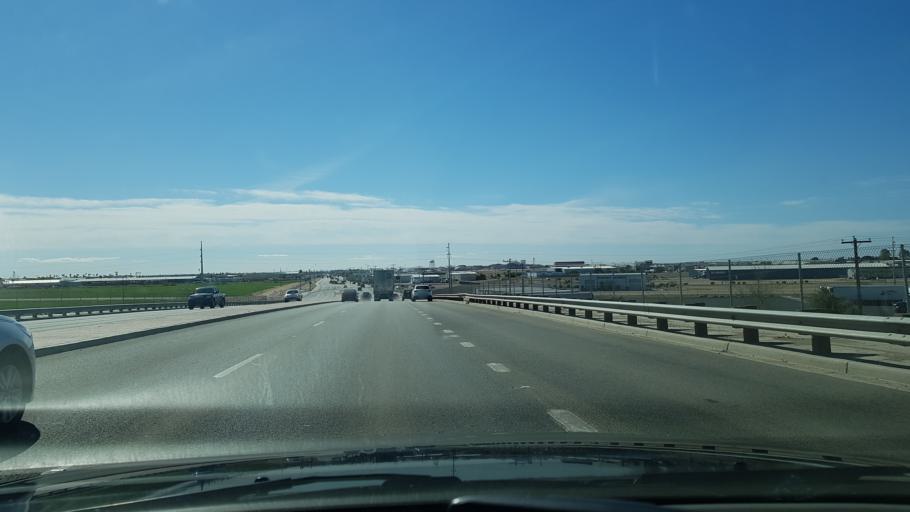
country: US
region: Arizona
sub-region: Yuma County
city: Yuma
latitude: 32.6832
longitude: -114.5817
